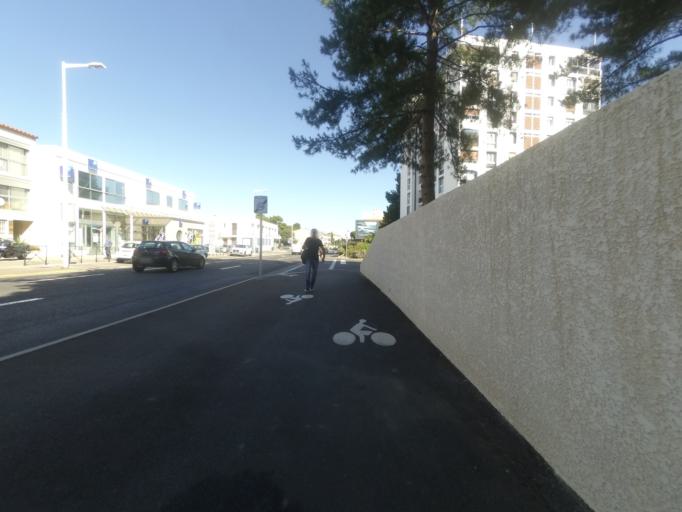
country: FR
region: Languedoc-Roussillon
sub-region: Departement des Pyrenees-Orientales
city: Perpignan
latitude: 42.6862
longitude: 2.9020
